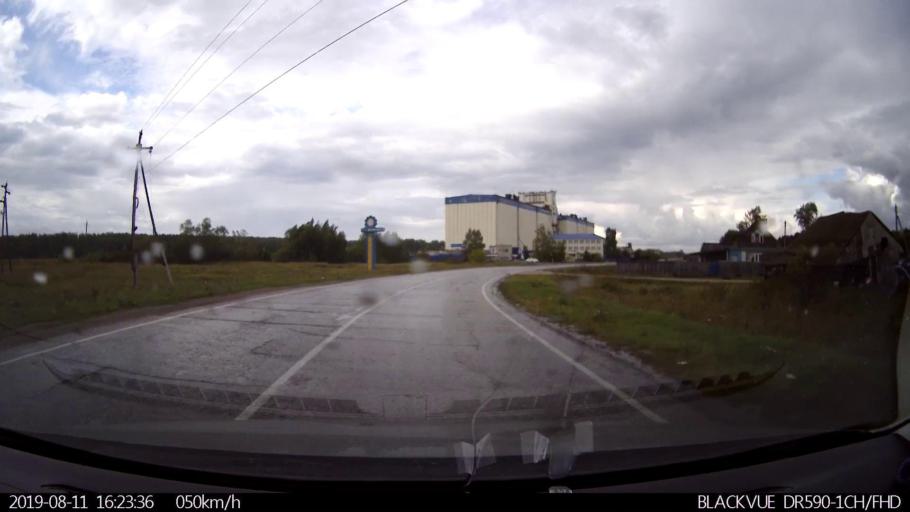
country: RU
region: Ulyanovsk
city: Mayna
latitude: 54.0962
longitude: 47.5884
